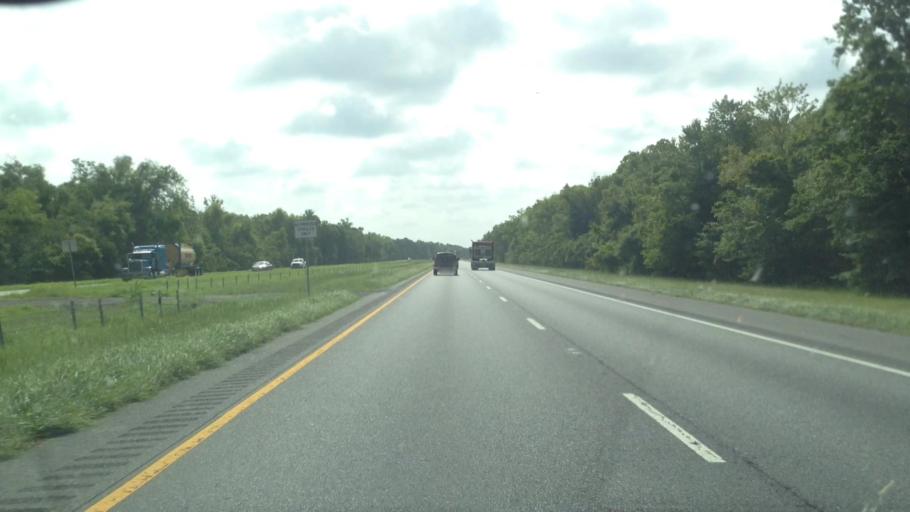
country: US
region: Louisiana
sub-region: Ascension Parish
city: Sorrento
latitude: 30.1508
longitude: -90.7891
